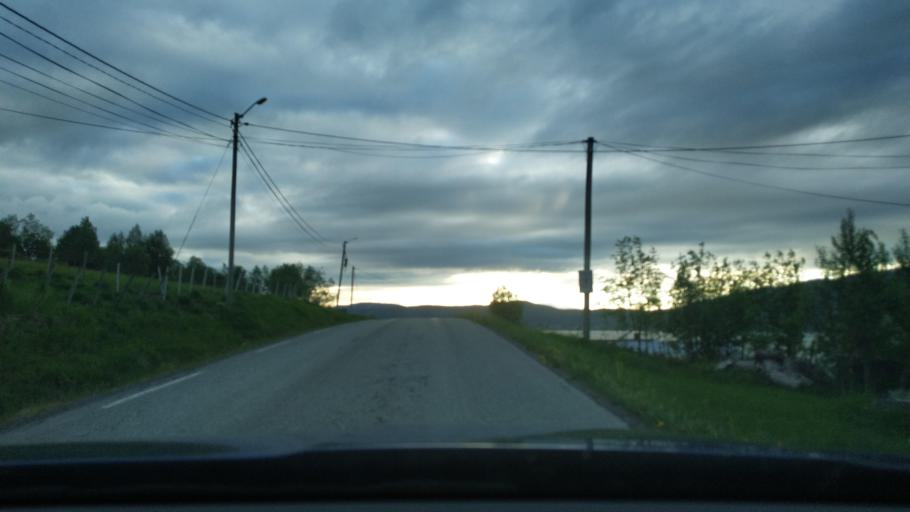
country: NO
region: Troms
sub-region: Tranoy
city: Vangsvika
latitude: 69.1269
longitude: 17.8507
